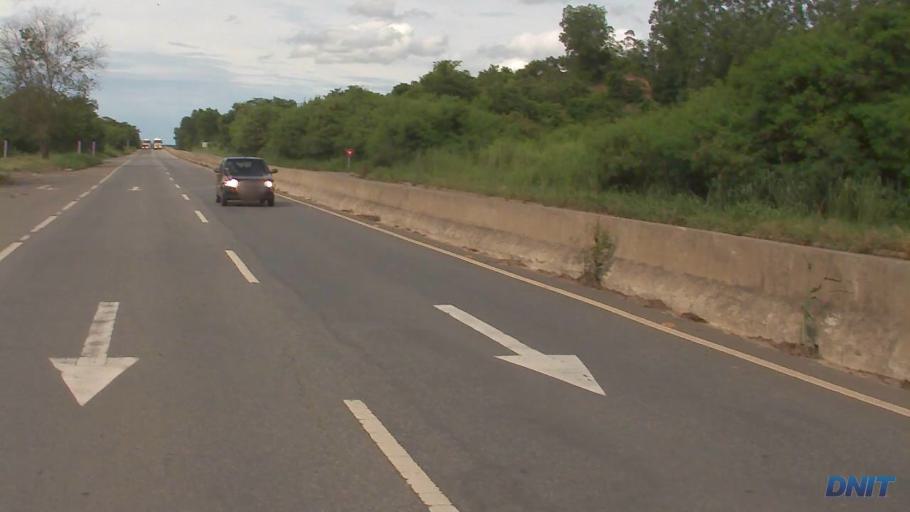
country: BR
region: Minas Gerais
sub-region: Ipaba
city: Ipaba
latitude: -19.3208
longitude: -42.4056
